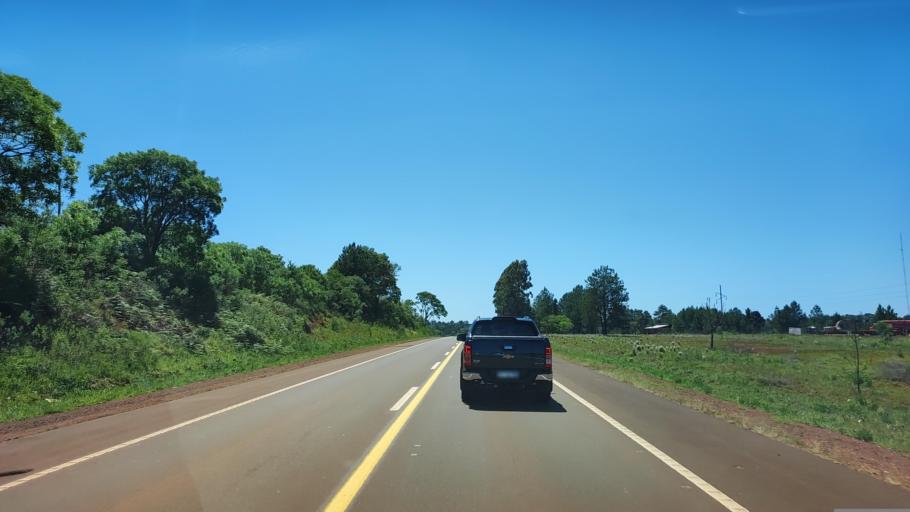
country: AR
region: Misiones
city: Aristobulo del Valle
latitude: -27.0864
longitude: -54.7940
